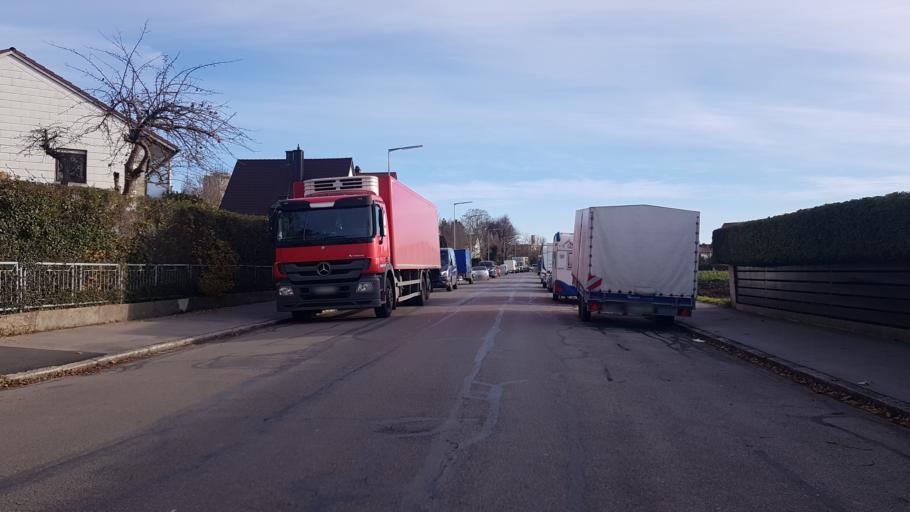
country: DE
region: Bavaria
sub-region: Upper Bavaria
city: Oberschleissheim
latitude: 48.2120
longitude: 11.5372
